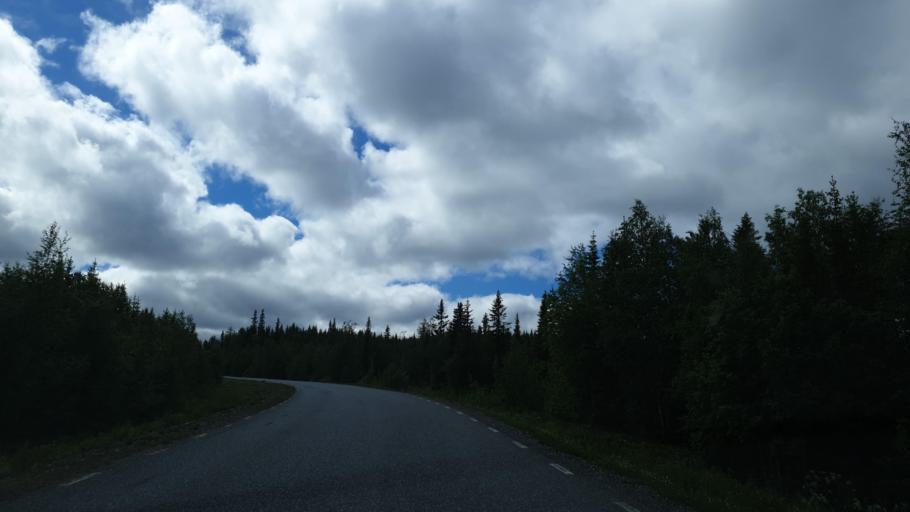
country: SE
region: Vaesterbotten
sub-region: Vilhelmina Kommun
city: Sjoberg
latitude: 65.2047
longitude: 15.9798
